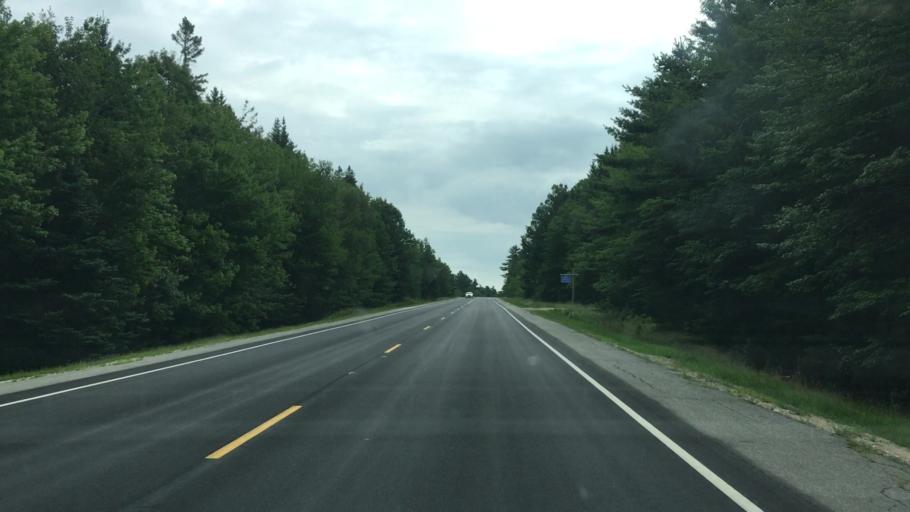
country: US
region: Maine
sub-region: Washington County
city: Addison
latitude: 44.9075
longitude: -67.8363
